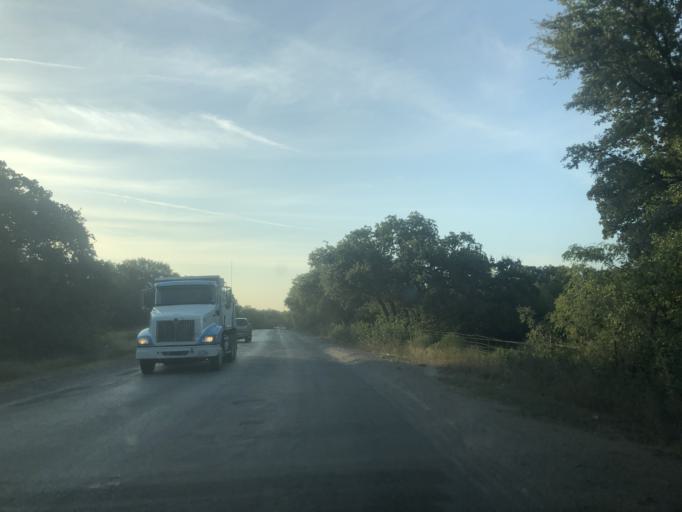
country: US
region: Texas
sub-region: Tarrant County
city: Lakeside
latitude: 32.7880
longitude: -97.4896
